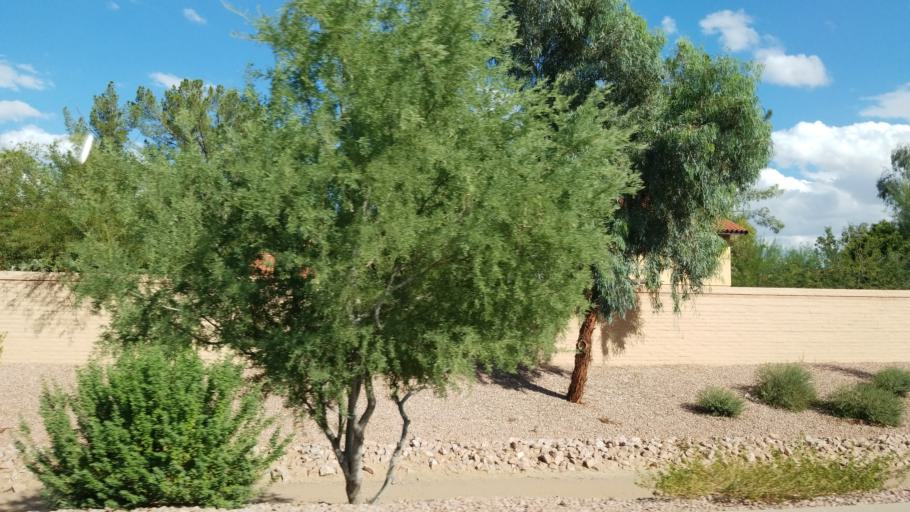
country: US
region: Arizona
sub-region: Maricopa County
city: Scottsdale
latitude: 33.5704
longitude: -111.8739
